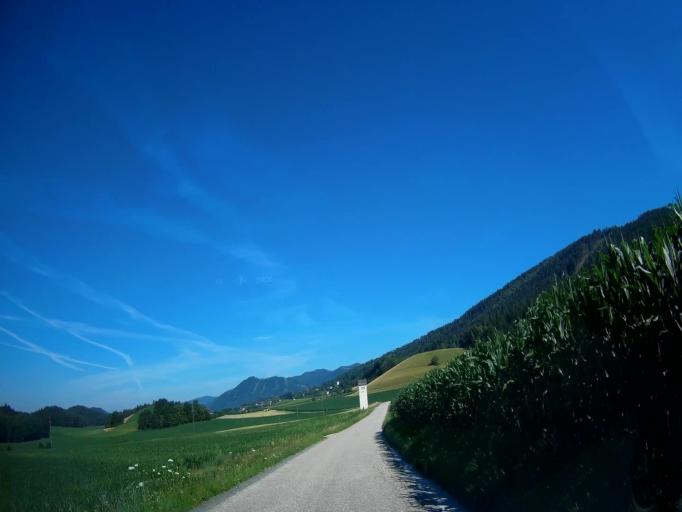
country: AT
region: Carinthia
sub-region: Politischer Bezirk Klagenfurt Land
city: Poggersdorf
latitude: 46.6696
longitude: 14.5299
